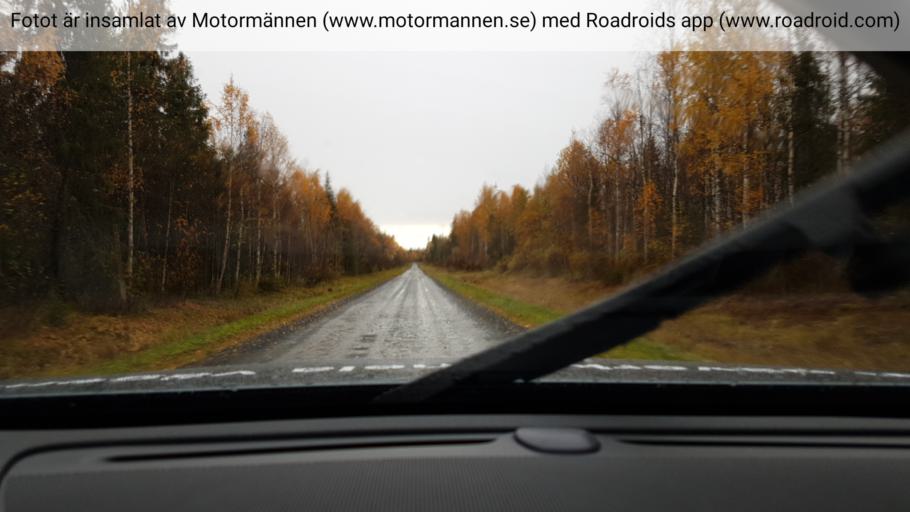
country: SE
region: Norrbotten
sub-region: Pajala Kommun
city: Pajala
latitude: 66.9660
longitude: 22.9319
